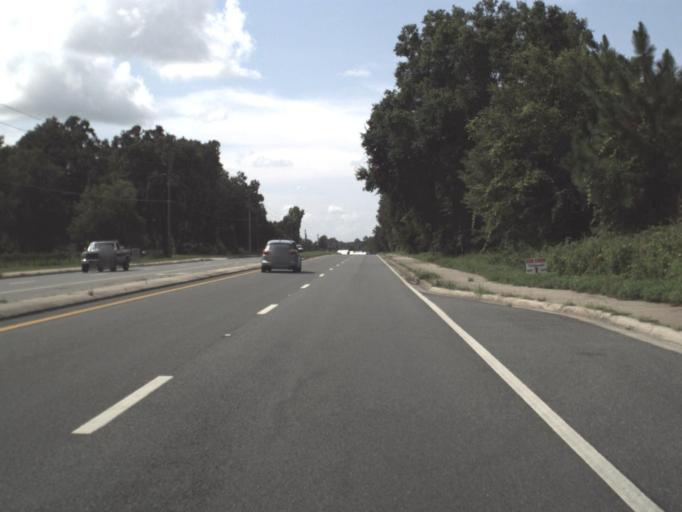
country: US
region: Florida
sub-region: Citrus County
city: Inverness Highlands South
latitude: 28.8016
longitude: -82.3093
